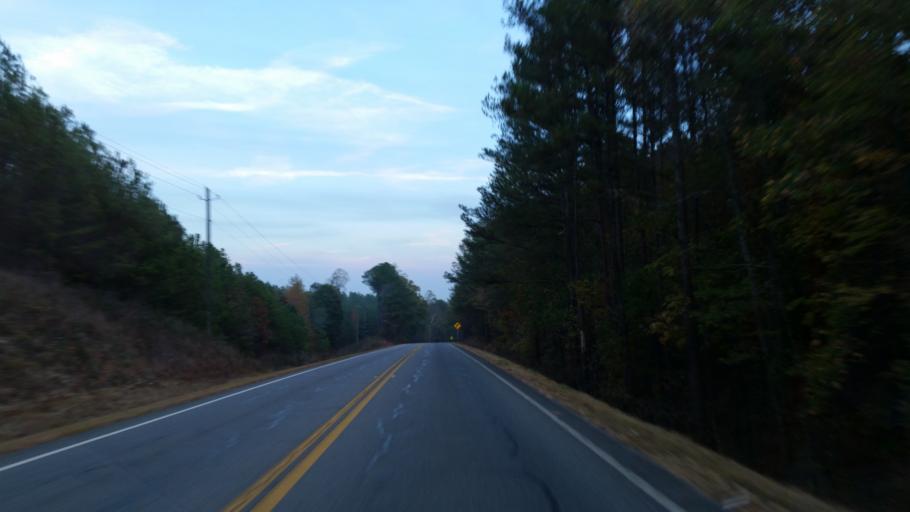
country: US
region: Georgia
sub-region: Murray County
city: Chatsworth
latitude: 34.5919
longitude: -84.7294
